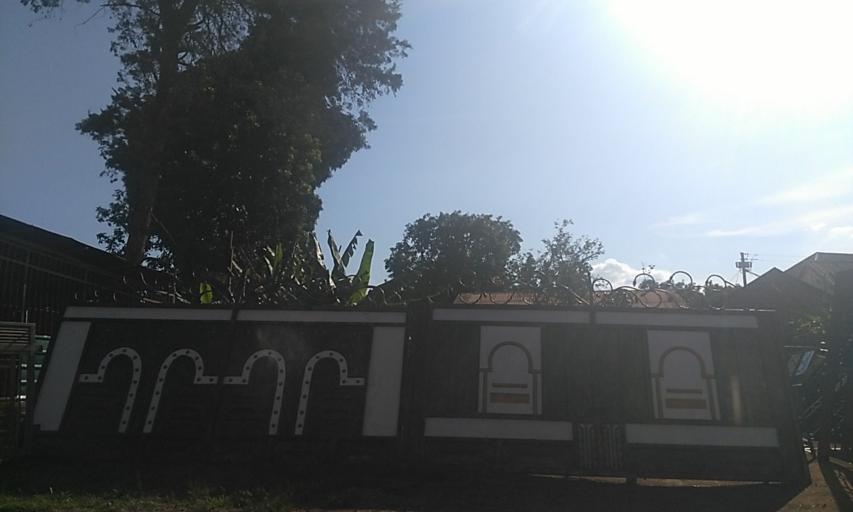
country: UG
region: Central Region
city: Kampala Central Division
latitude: 0.3245
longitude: 32.5402
